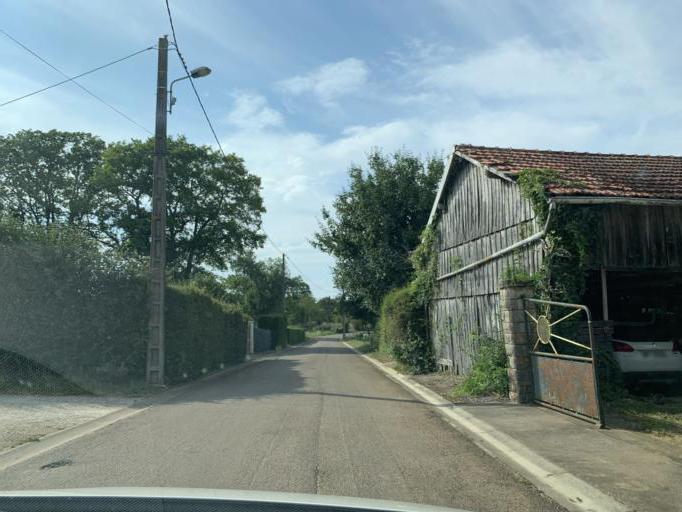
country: FR
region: Bourgogne
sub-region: Departement de l'Yonne
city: Fontenailles
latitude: 47.5180
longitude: 3.4274
